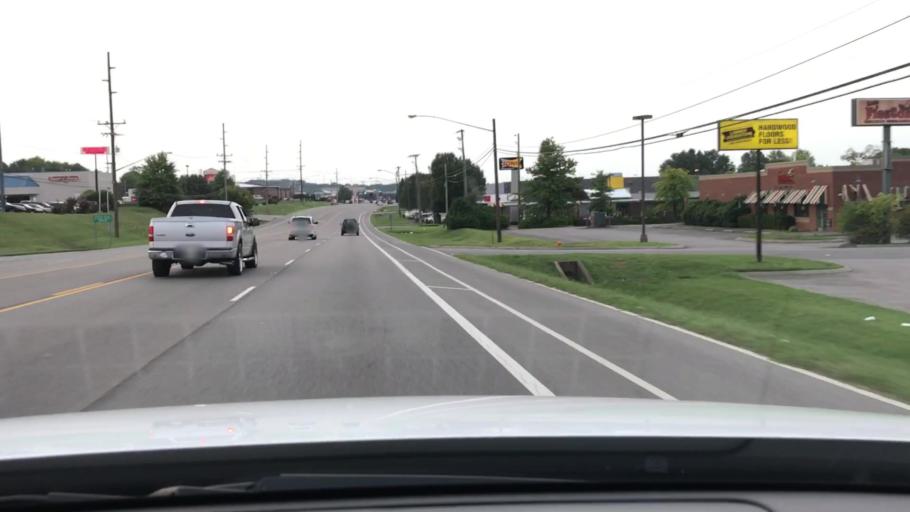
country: US
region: Tennessee
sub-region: Davidson County
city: Goodlettsville
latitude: 36.2903
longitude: -86.7037
